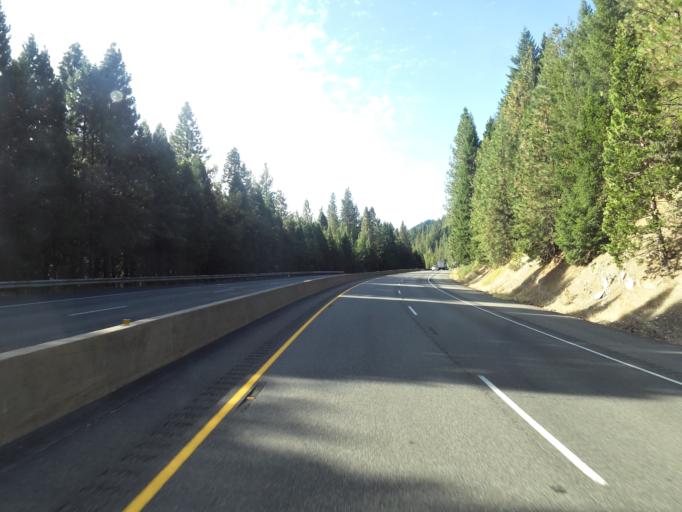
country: US
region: California
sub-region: Siskiyou County
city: Dunsmuir
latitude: 41.1415
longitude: -122.3183
